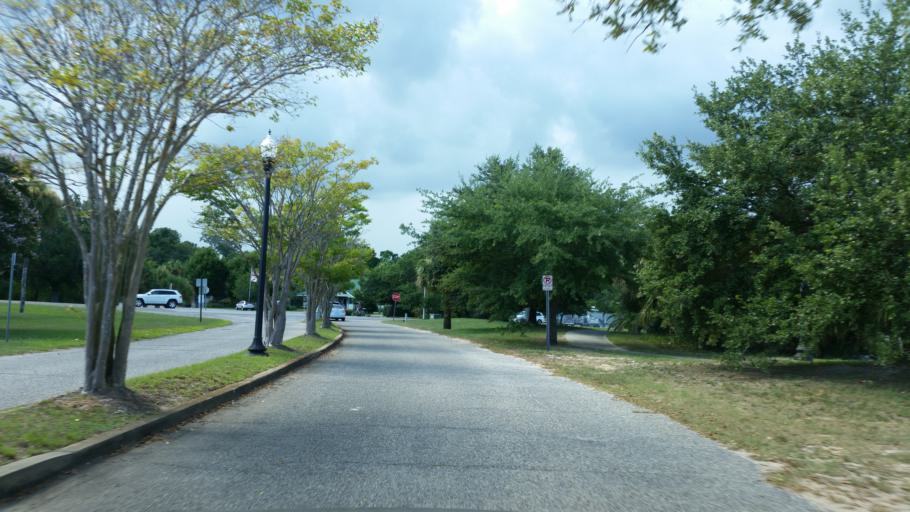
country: US
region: Florida
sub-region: Escambia County
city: East Pensacola Heights
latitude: 30.4182
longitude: -87.1935
